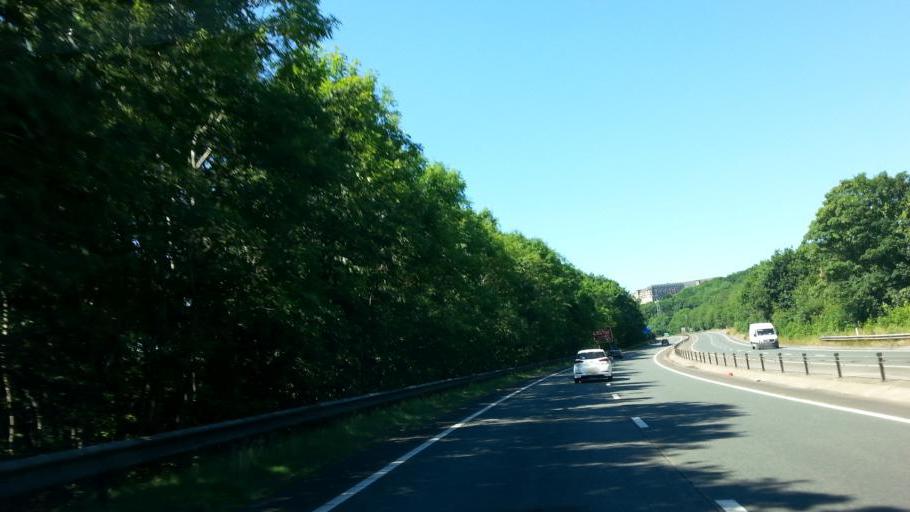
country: GB
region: Wales
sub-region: Newport
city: Langstone
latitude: 51.6066
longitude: -2.9168
